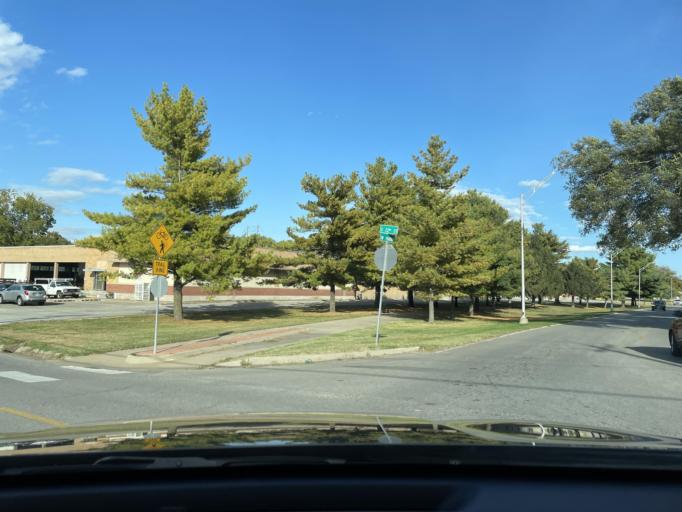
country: US
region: Missouri
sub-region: Buchanan County
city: Saint Joseph
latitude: 39.7372
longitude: -94.8341
